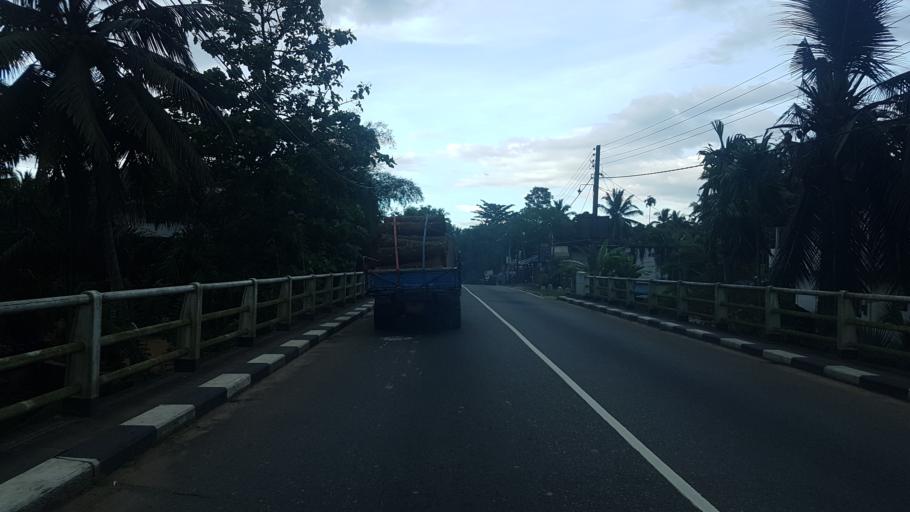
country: LK
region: Western
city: Hanwella Ihala
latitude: 7.0205
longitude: 80.2628
